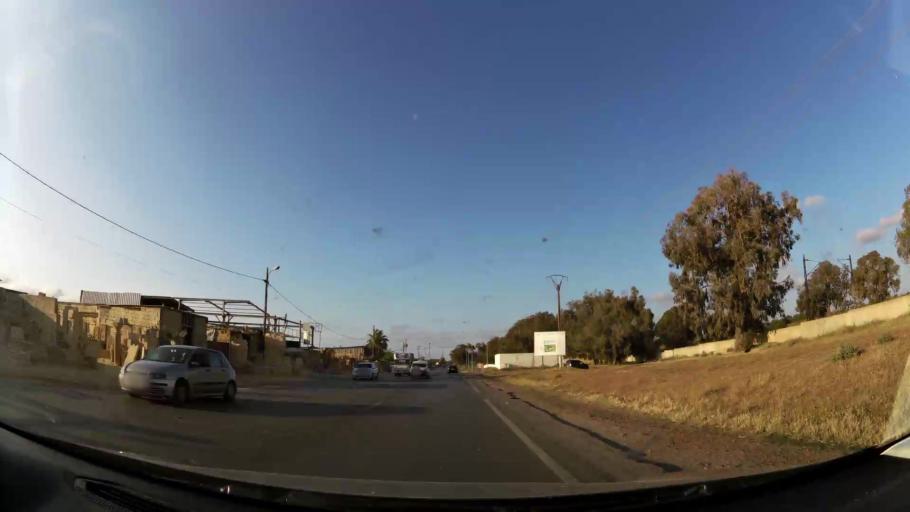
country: MA
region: Rabat-Sale-Zemmour-Zaer
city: Sale
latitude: 34.0983
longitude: -6.7608
